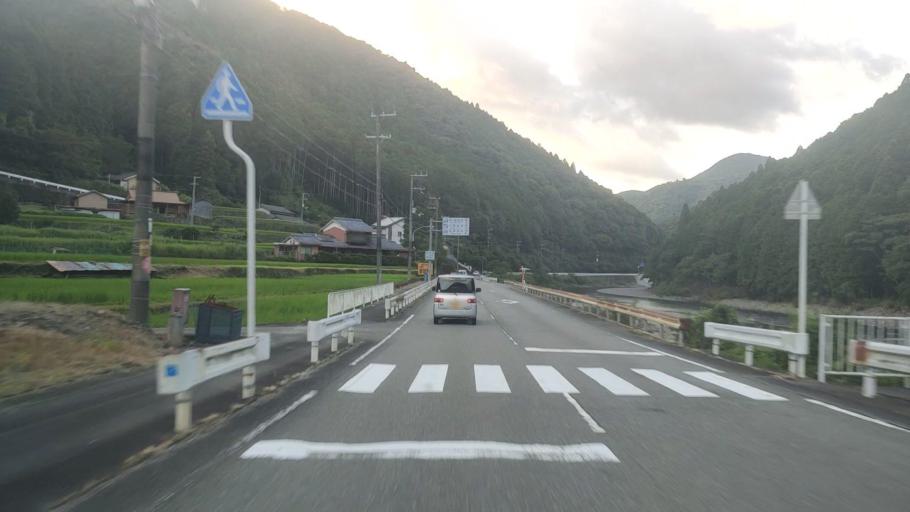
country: JP
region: Wakayama
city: Tanabe
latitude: 33.7834
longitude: 135.5055
